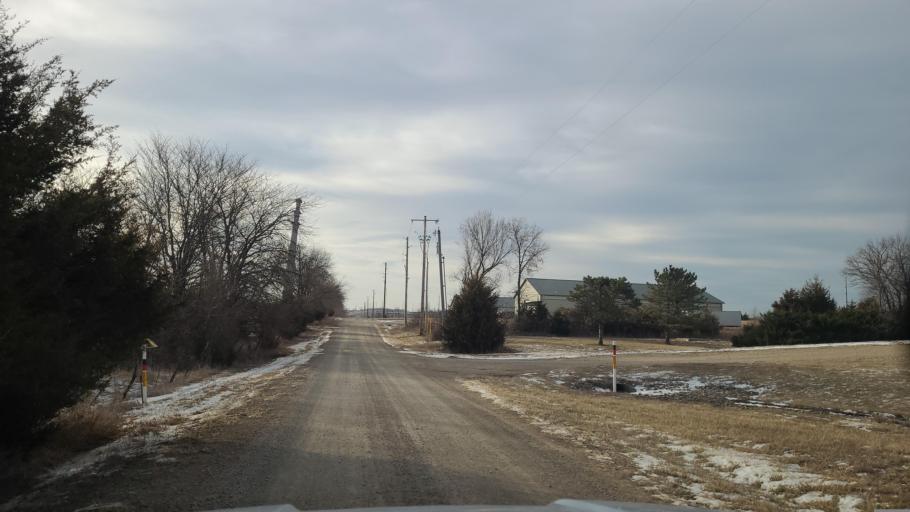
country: US
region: Kansas
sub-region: Douglas County
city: Lawrence
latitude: 38.9868
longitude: -95.3353
